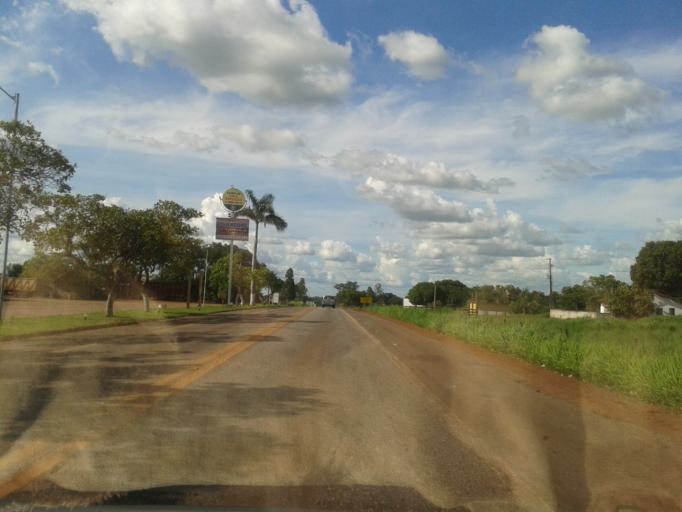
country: BR
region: Goias
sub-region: Mozarlandia
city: Mozarlandia
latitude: -14.7637
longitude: -50.5385
